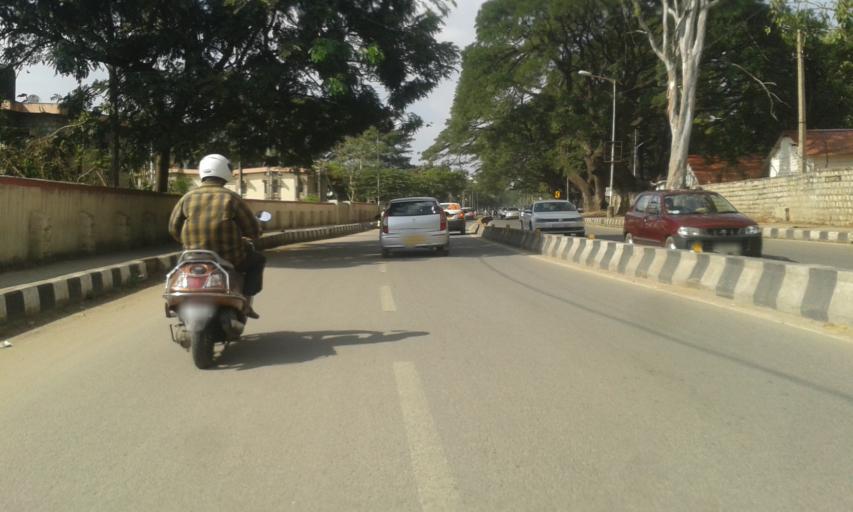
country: IN
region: Karnataka
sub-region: Bangalore Urban
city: Bangalore
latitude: 12.9587
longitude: 77.6206
